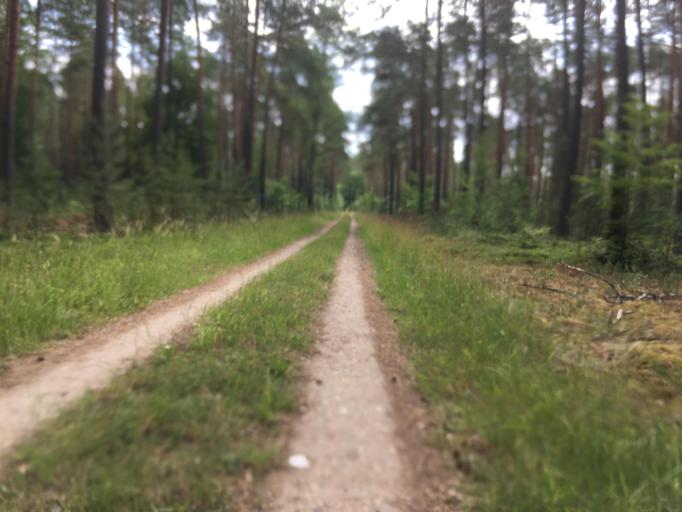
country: DE
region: Brandenburg
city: Joachimsthal
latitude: 53.0082
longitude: 13.7453
